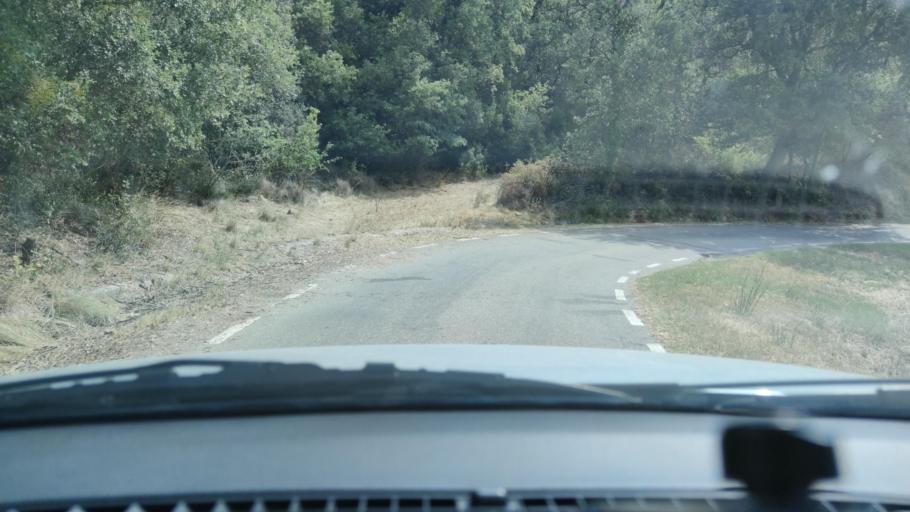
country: ES
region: Catalonia
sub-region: Provincia de Lleida
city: Ager
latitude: 42.0134
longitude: 0.8301
